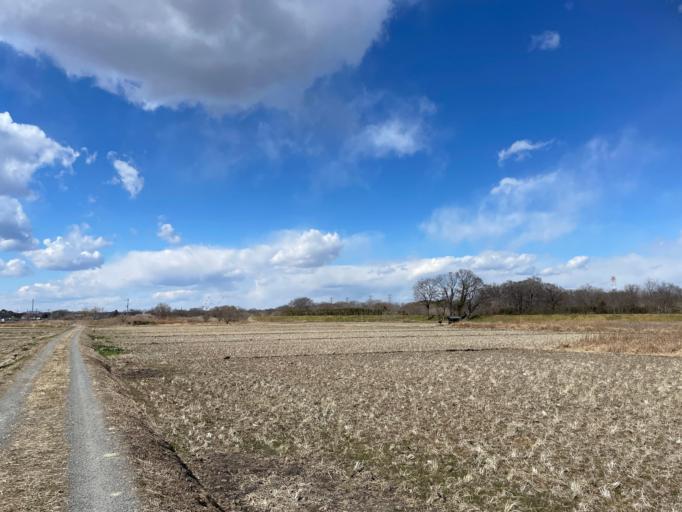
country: JP
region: Saitama
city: Sakado
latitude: 36.0131
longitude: 139.3921
